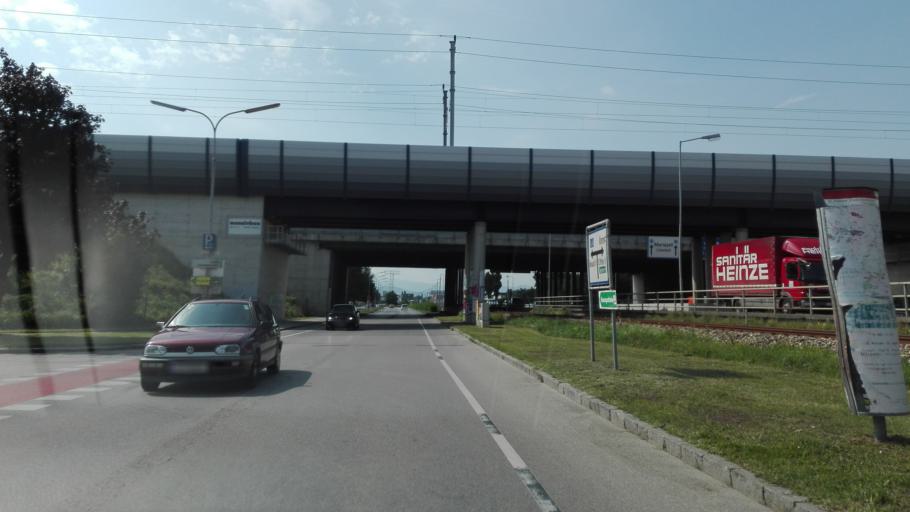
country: AT
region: Lower Austria
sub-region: Sankt Polten Stadt
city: Sankt Poelten
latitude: 48.1779
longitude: 15.6162
